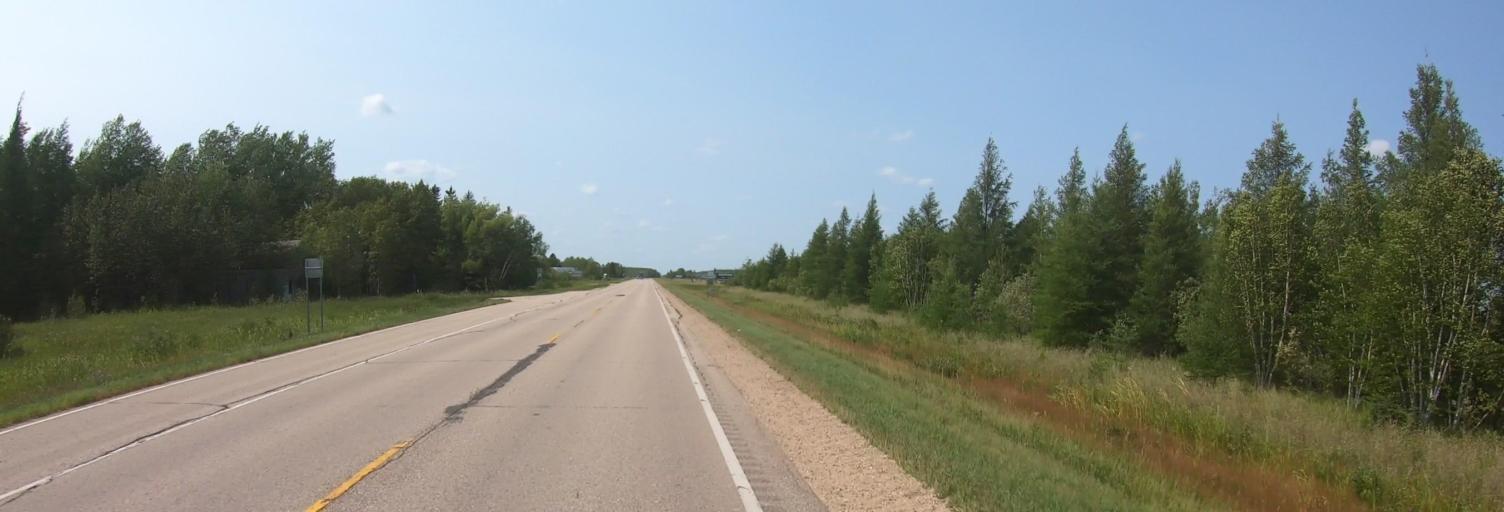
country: US
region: Minnesota
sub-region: Lake of the Woods County
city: Baudette
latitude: 48.7400
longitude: -94.8380
